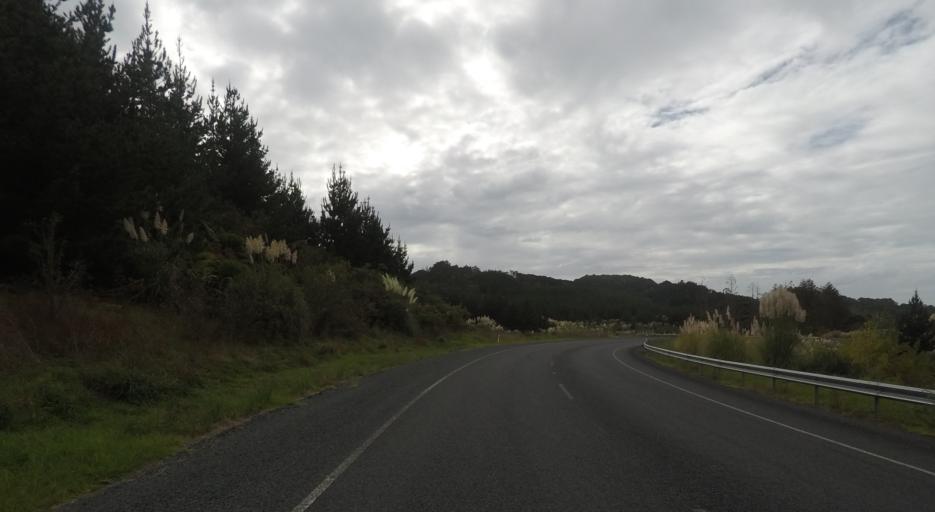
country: NZ
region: Auckland
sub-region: Auckland
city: Rothesay Bay
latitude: -36.6513
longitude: 174.7089
